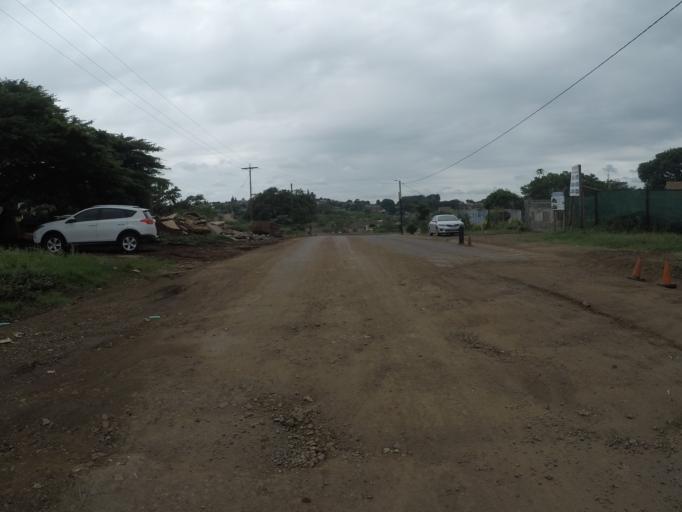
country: ZA
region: KwaZulu-Natal
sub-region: uThungulu District Municipality
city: Empangeni
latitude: -28.7724
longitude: 31.8554
